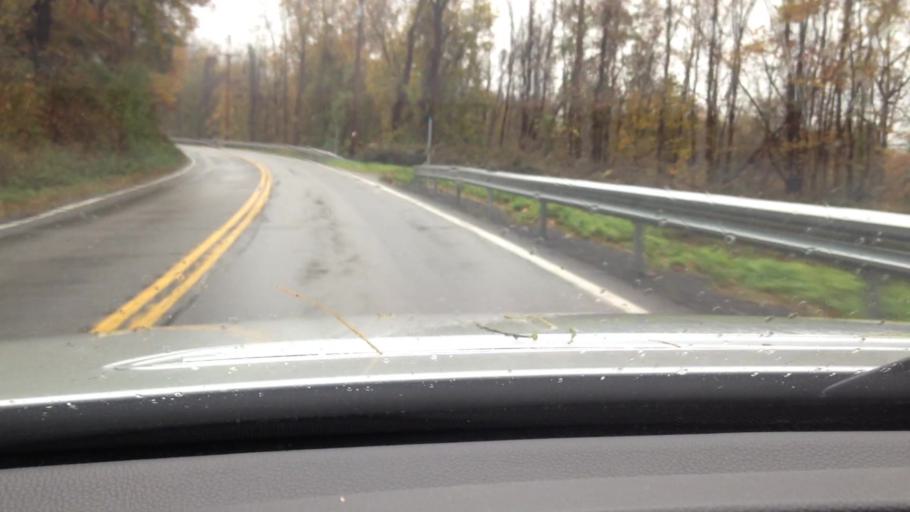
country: US
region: New York
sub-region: Dutchess County
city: Beacon
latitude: 41.4720
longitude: -73.9754
